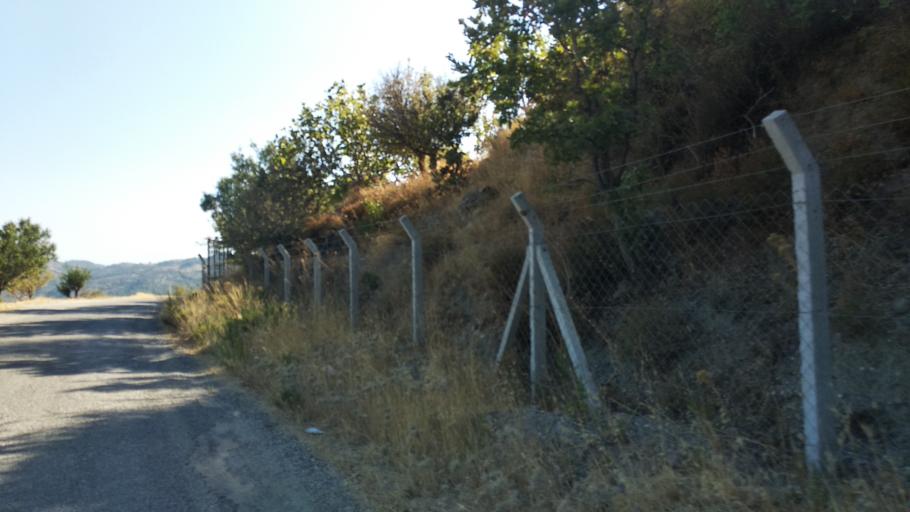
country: TR
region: Izmir
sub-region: Seferihisar
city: Seferhisar
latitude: 38.3212
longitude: 26.9298
